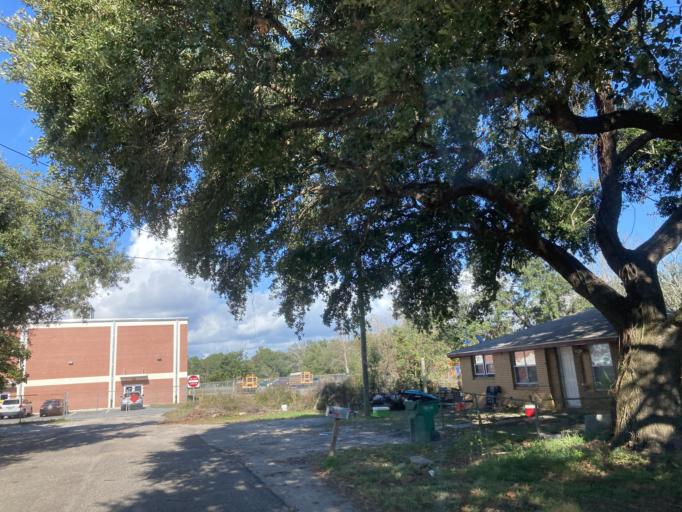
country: US
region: Mississippi
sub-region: Harrison County
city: West Gulfport
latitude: 30.4053
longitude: -89.0993
